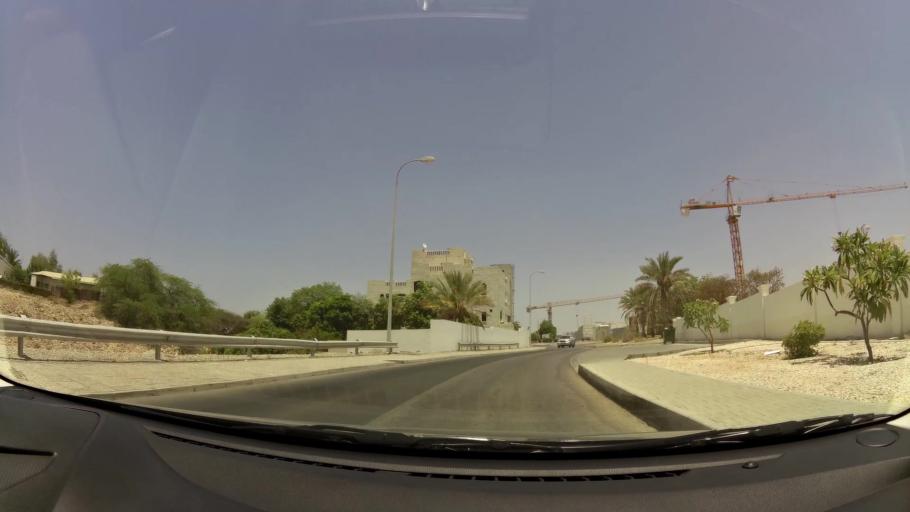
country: OM
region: Muhafazat Masqat
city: Muscat
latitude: 23.6254
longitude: 58.5012
